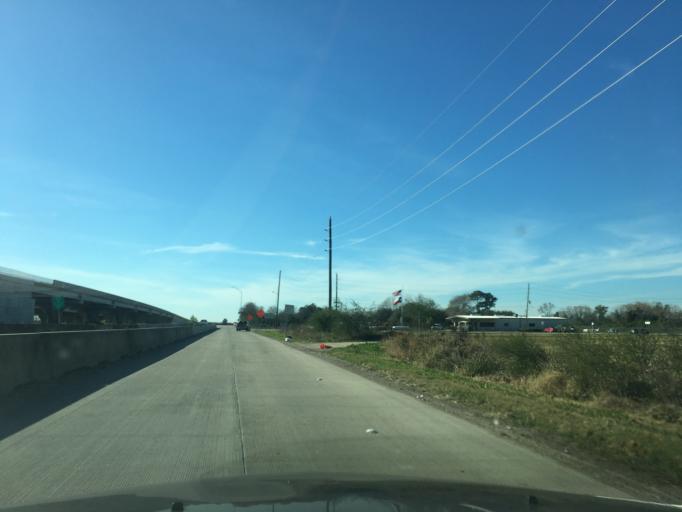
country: US
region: Texas
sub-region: Fort Bend County
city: Rosenberg
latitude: 29.5323
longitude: -95.8176
